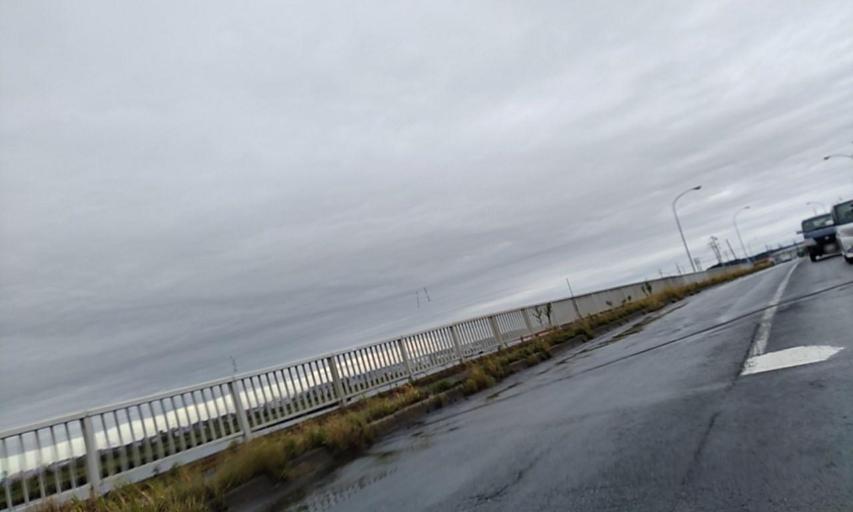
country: JP
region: Hokkaido
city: Kushiro
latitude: 43.0000
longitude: 144.4140
